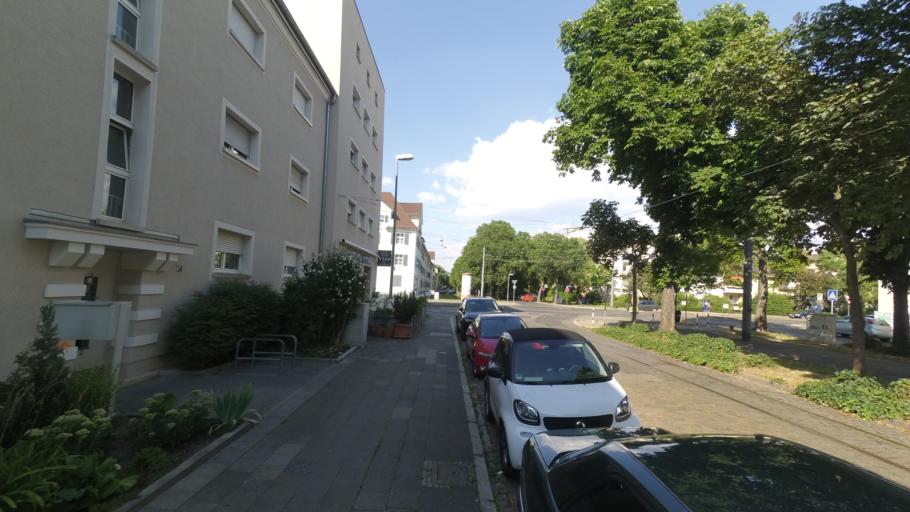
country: DE
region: Rheinland-Pfalz
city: Ludwigshafen am Rhein
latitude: 49.4918
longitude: 8.4201
